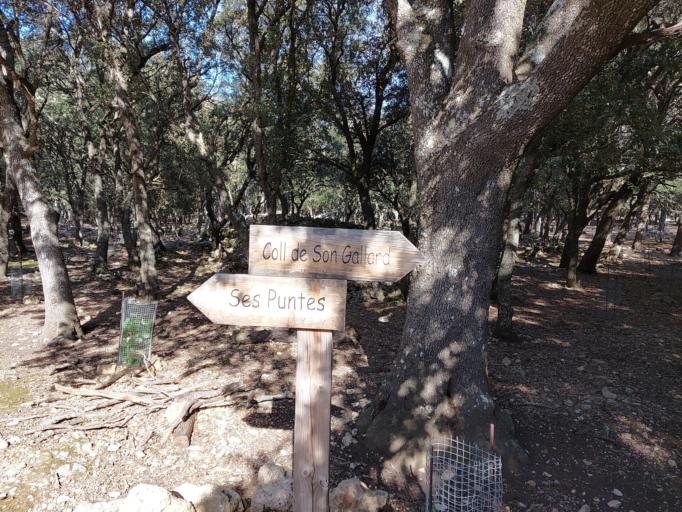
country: ES
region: Balearic Islands
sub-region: Illes Balears
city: Valldemossa
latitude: 39.7228
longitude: 2.6206
